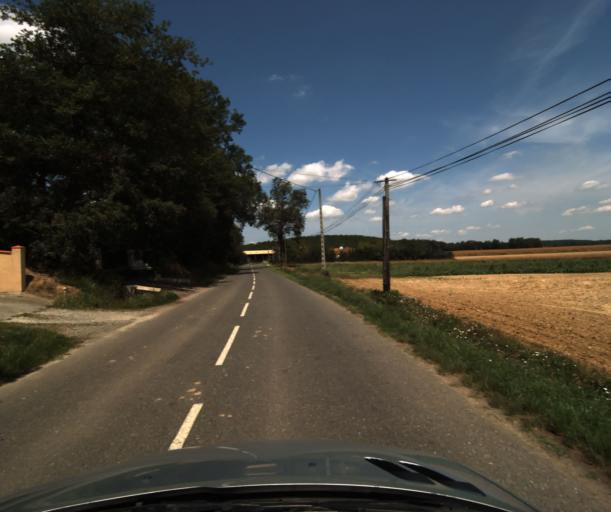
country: FR
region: Midi-Pyrenees
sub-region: Departement de la Haute-Garonne
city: Labastidette
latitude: 43.4740
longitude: 1.2171
